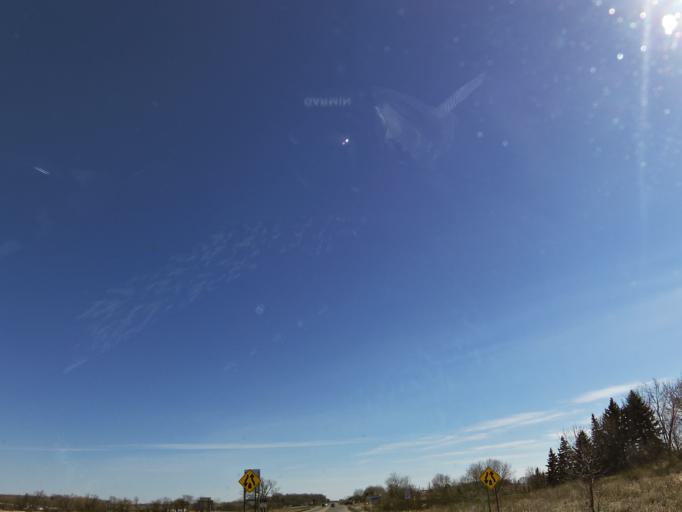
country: US
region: Minnesota
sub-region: Wright County
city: Buffalo
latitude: 45.1531
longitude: -93.8471
